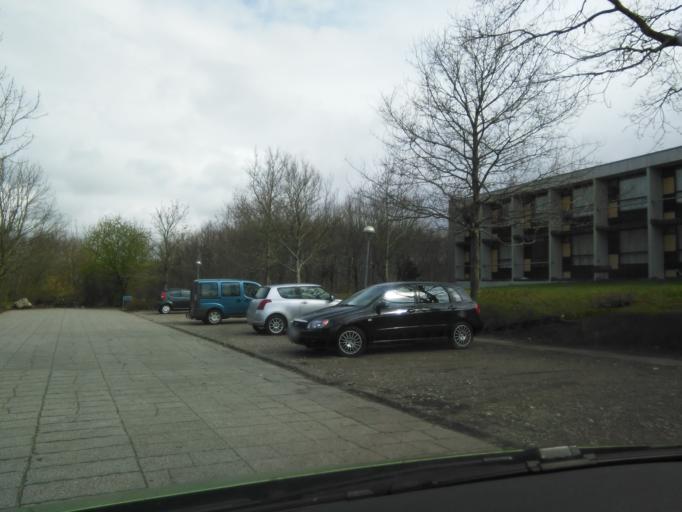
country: DK
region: Central Jutland
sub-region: Arhus Kommune
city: Stavtrup
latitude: 56.1702
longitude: 10.1119
